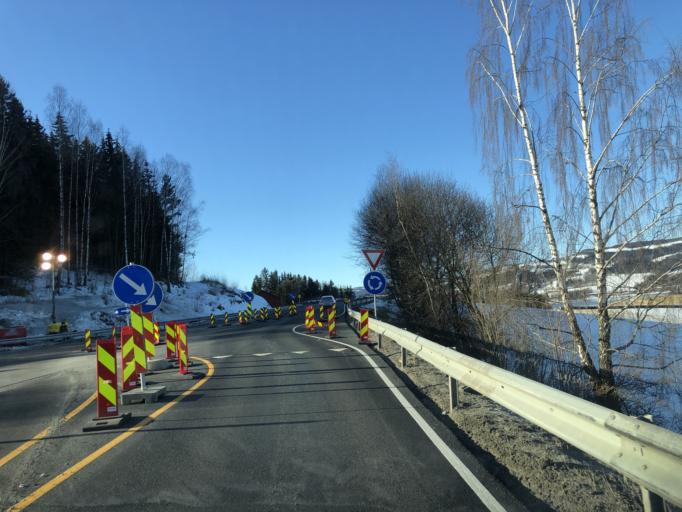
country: NO
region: Hedmark
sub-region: Ringsaker
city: Moelv
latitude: 60.9114
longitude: 10.7078
